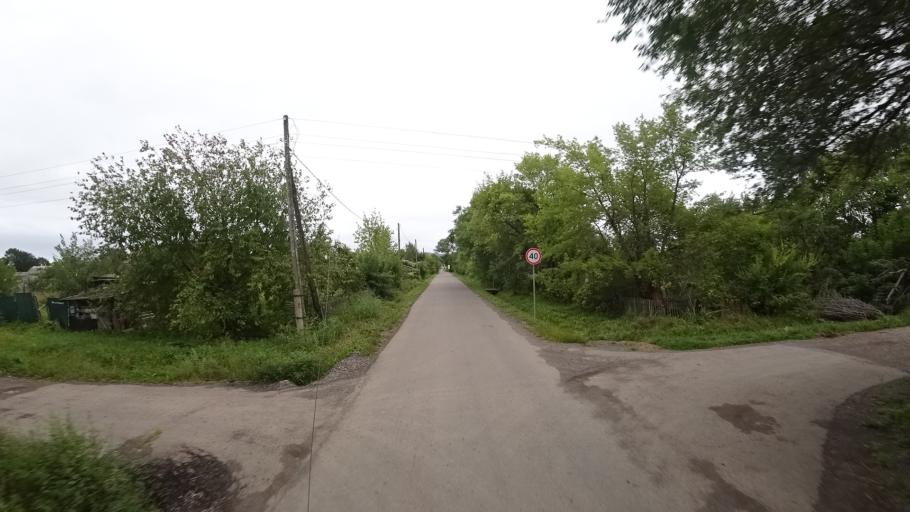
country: RU
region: Primorskiy
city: Chernigovka
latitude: 44.3374
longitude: 132.5392
